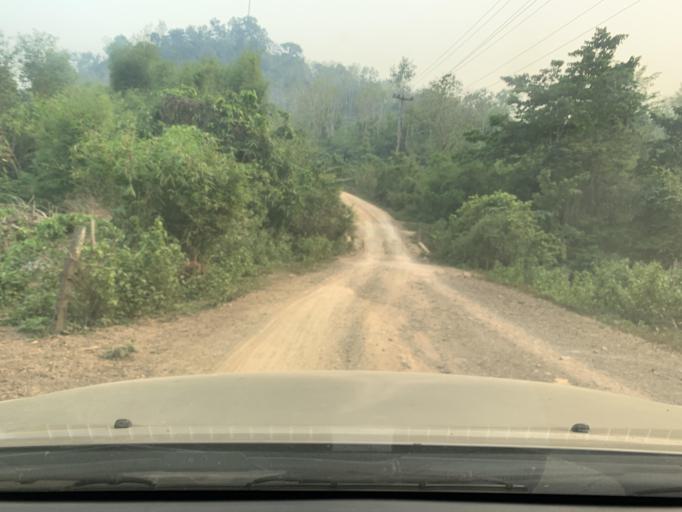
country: LA
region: Louangphabang
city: Louangphabang
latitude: 19.9251
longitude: 102.0745
